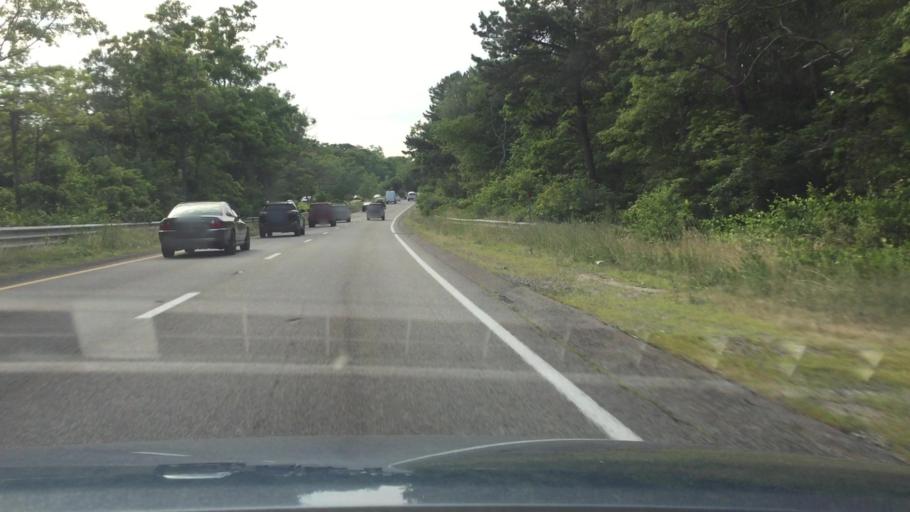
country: US
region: Massachusetts
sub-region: Barnstable County
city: Sandwich
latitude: 41.7411
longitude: -70.5043
